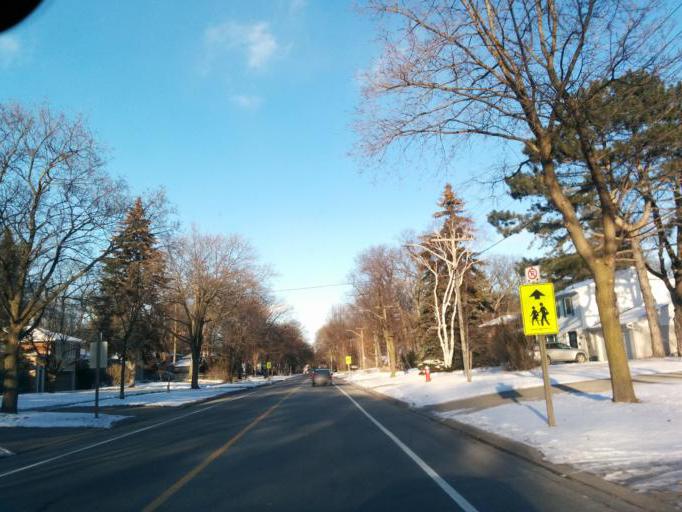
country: CA
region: Ontario
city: Mississauga
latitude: 43.5281
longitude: -79.6330
